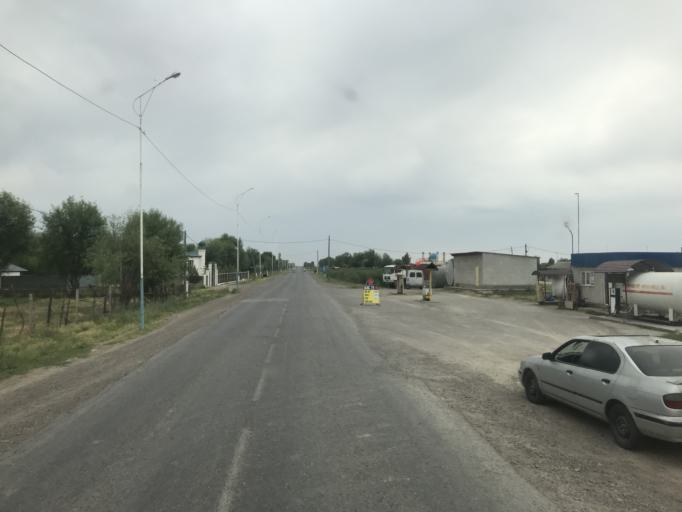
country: KZ
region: Ongtustik Qazaqstan
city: Asykata
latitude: 40.9337
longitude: 68.4091
